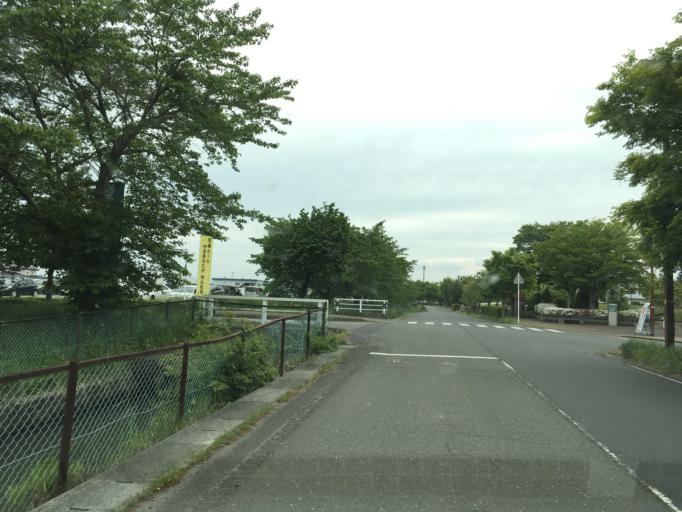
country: JP
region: Miyagi
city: Wakuya
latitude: 38.7144
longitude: 141.2398
